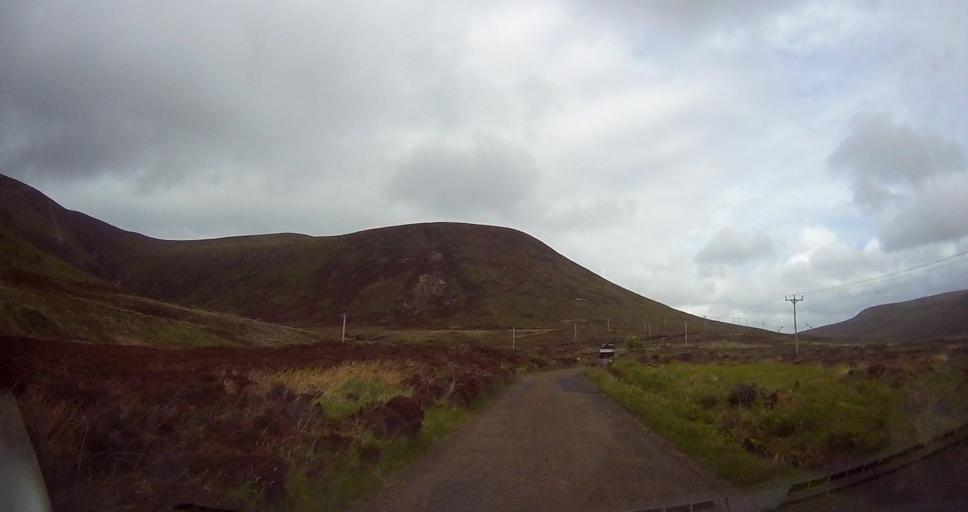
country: GB
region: Scotland
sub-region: Orkney Islands
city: Stromness
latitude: 58.8849
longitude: -3.3321
